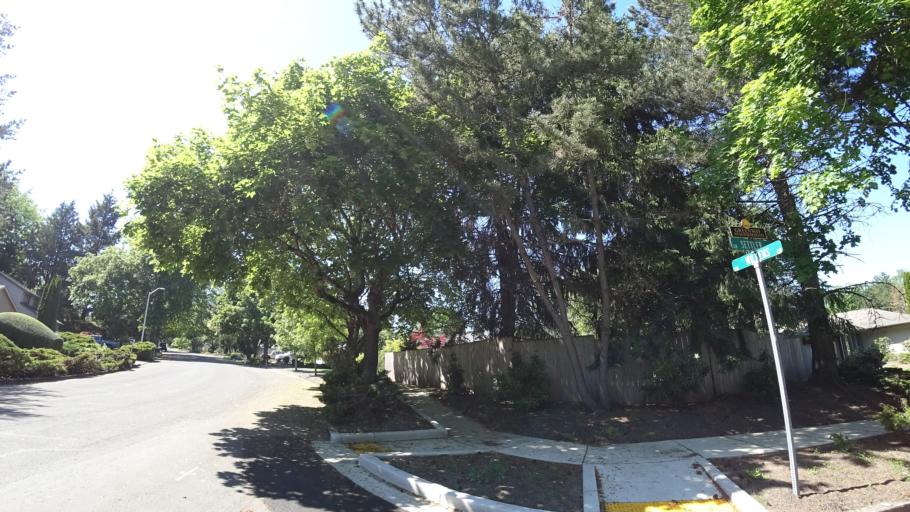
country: US
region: Oregon
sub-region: Washington County
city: Tigard
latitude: 45.4497
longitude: -122.7966
